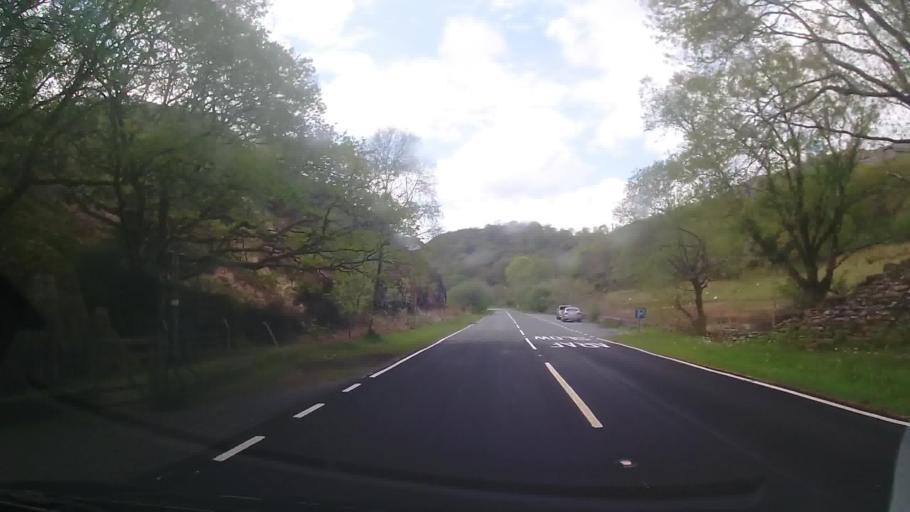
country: GB
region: Wales
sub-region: Gwynedd
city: Penrhyndeudraeth
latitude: 53.0236
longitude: -4.0706
